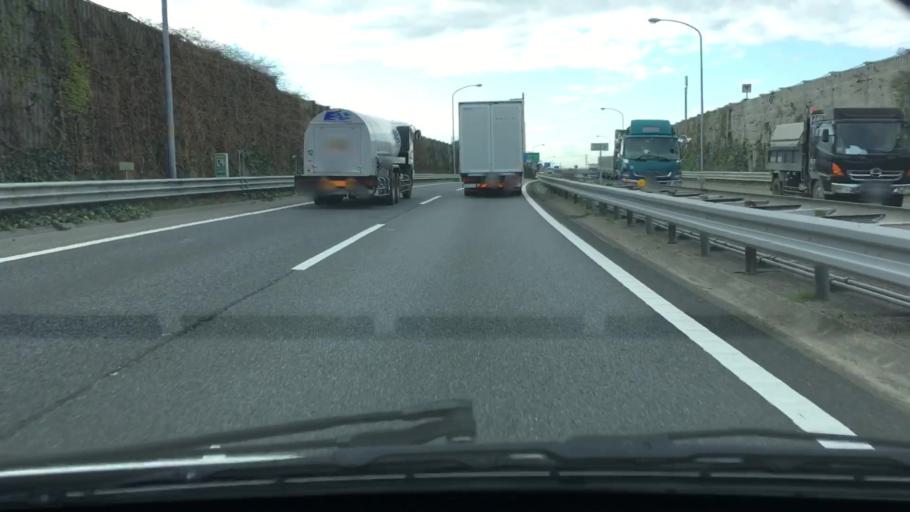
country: JP
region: Chiba
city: Chiba
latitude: 35.5792
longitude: 140.1476
